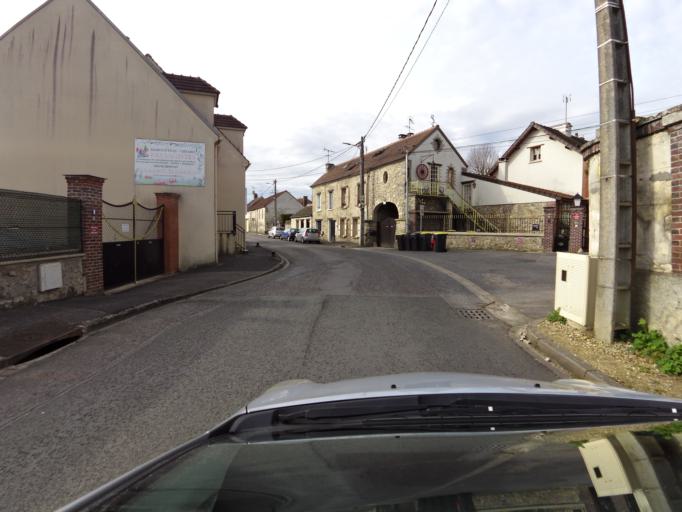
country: FR
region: Picardie
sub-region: Departement de l'Oise
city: Ver-sur-Launette
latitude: 49.1079
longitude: 2.6849
